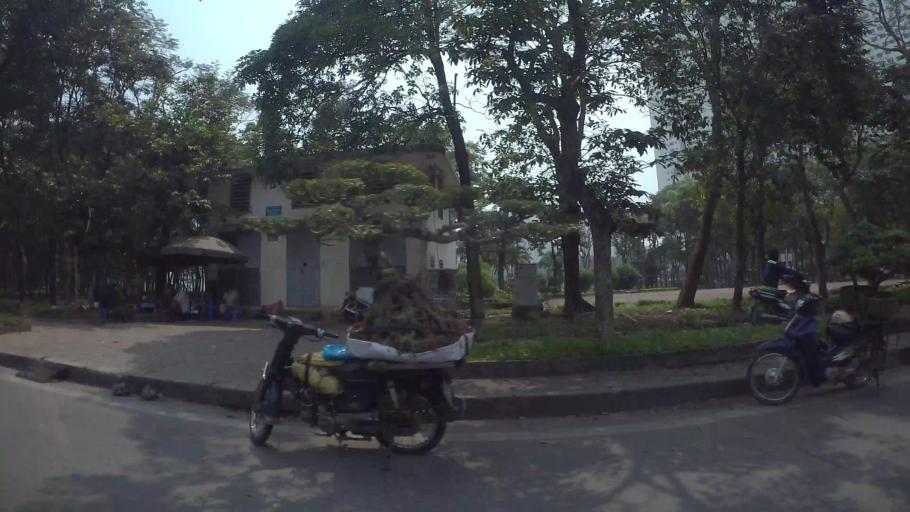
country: VN
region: Ha Noi
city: Van Dien
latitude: 20.9662
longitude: 105.8260
